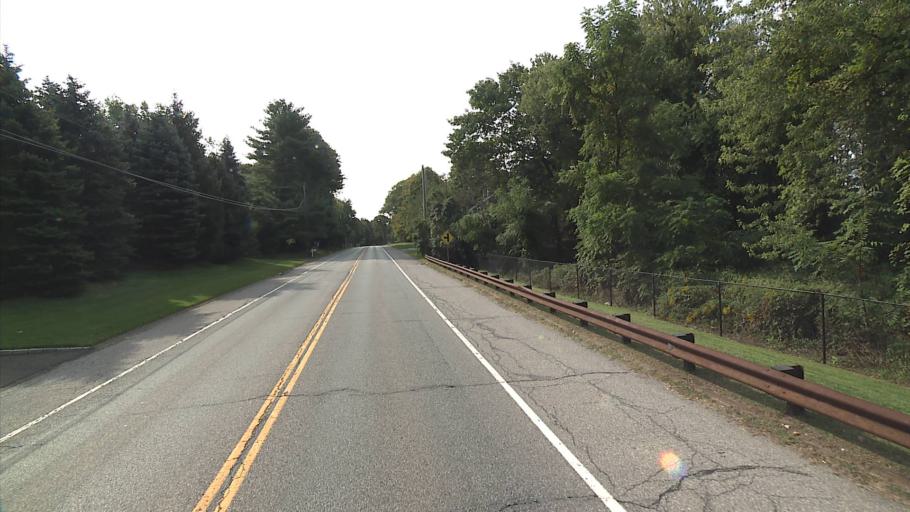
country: US
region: Connecticut
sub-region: Fairfield County
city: New Canaan
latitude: 41.1990
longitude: -73.5084
